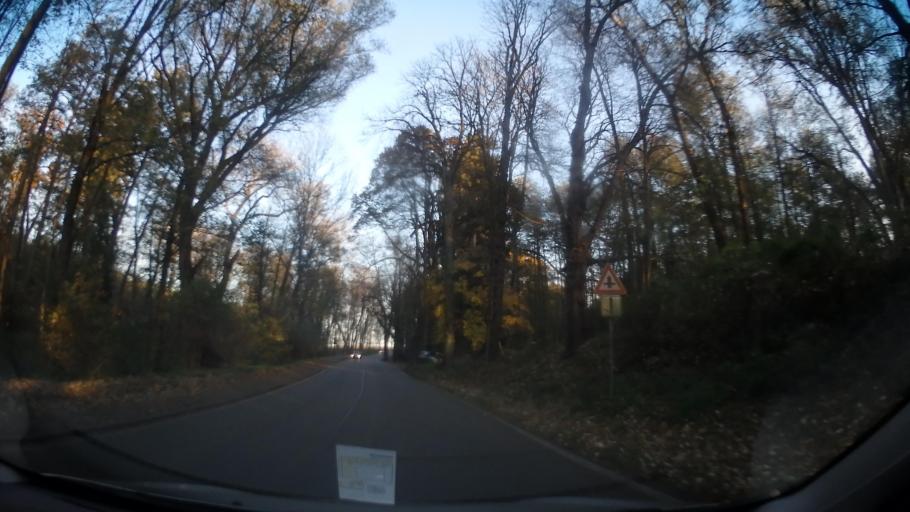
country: CZ
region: Central Bohemia
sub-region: Okres Benesov
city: Benesov
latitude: 49.7816
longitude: 14.6622
